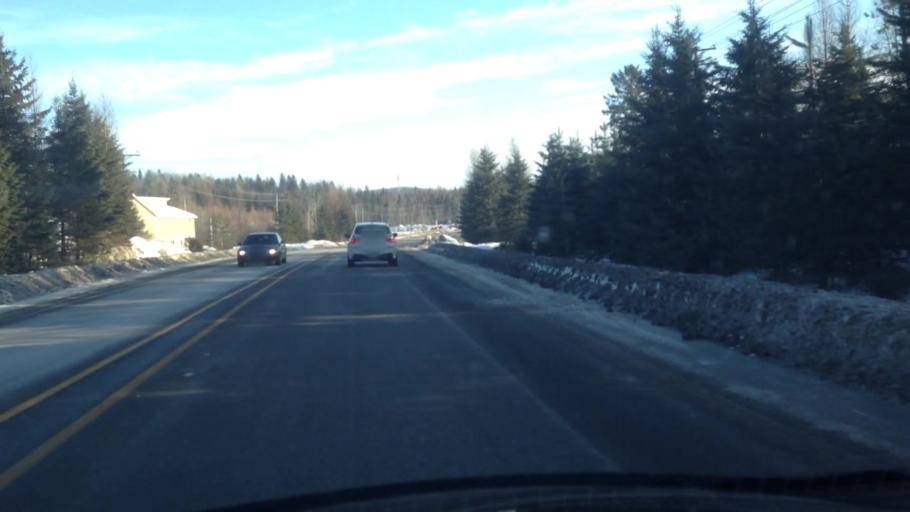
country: CA
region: Quebec
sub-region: Laurentides
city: Saint-Sauveur
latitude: 45.8944
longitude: -74.1993
